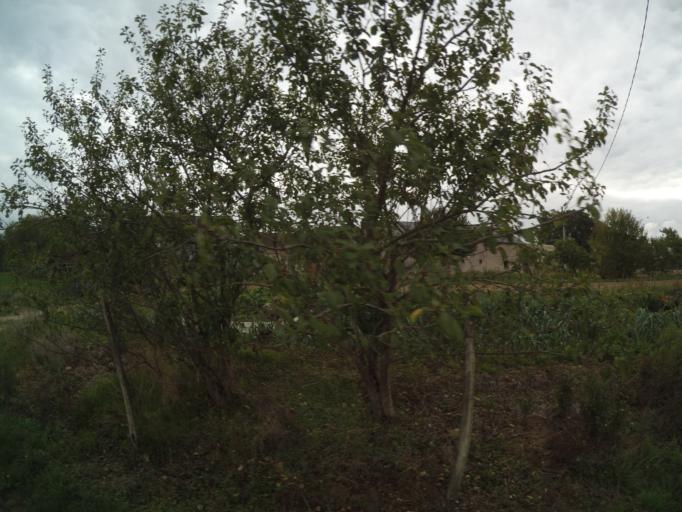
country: FR
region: Centre
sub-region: Departement d'Indre-et-Loire
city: Auzouer-en-Touraine
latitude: 47.4975
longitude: 0.9321
